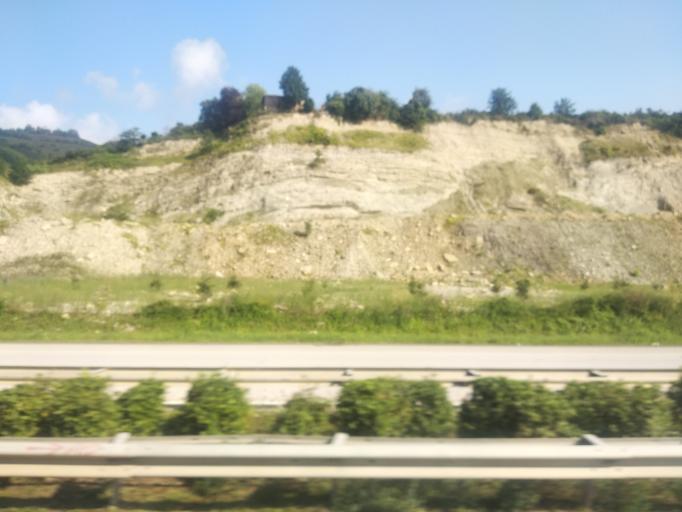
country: TR
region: Ordu
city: Ordu
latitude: 41.0013
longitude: 37.8237
